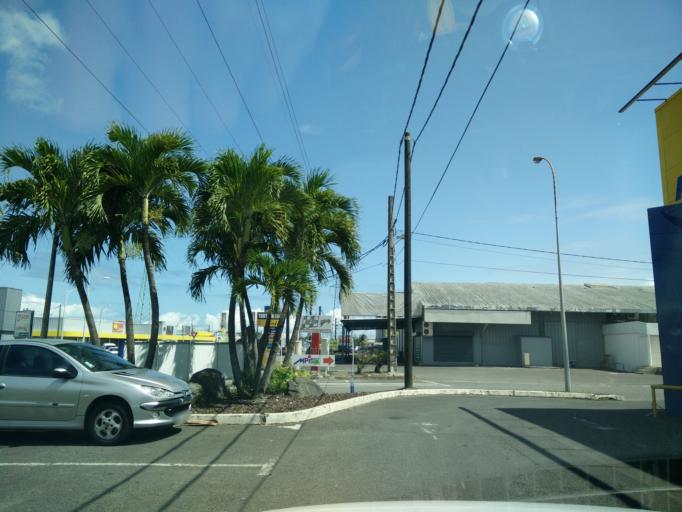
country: GP
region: Guadeloupe
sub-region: Guadeloupe
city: Pointe-a-Pitre
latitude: 16.2440
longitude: -61.5552
